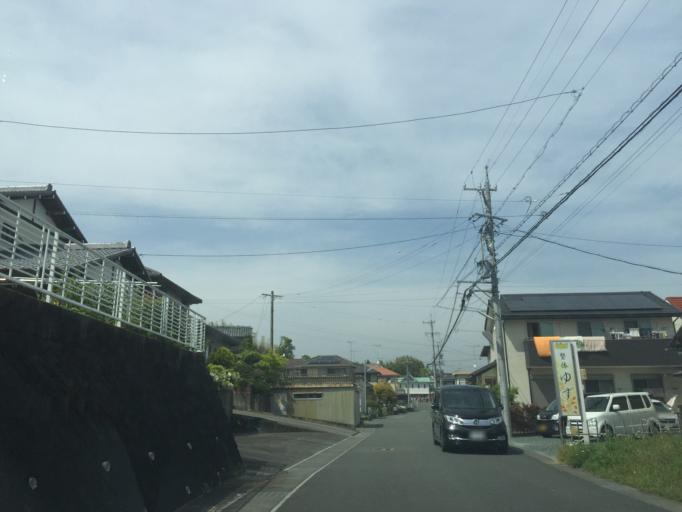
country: JP
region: Shizuoka
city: Kakegawa
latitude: 34.7818
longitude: 138.0269
